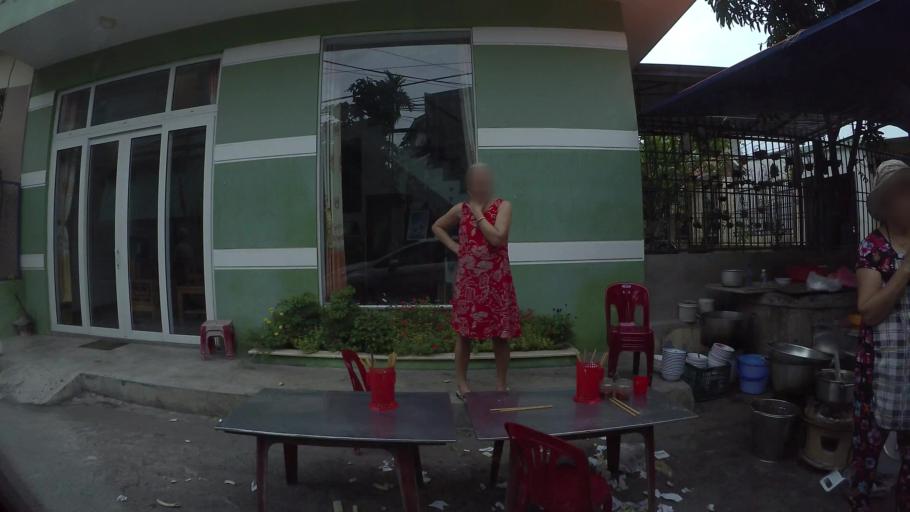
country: VN
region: Da Nang
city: Thanh Khe
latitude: 16.0711
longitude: 108.1833
